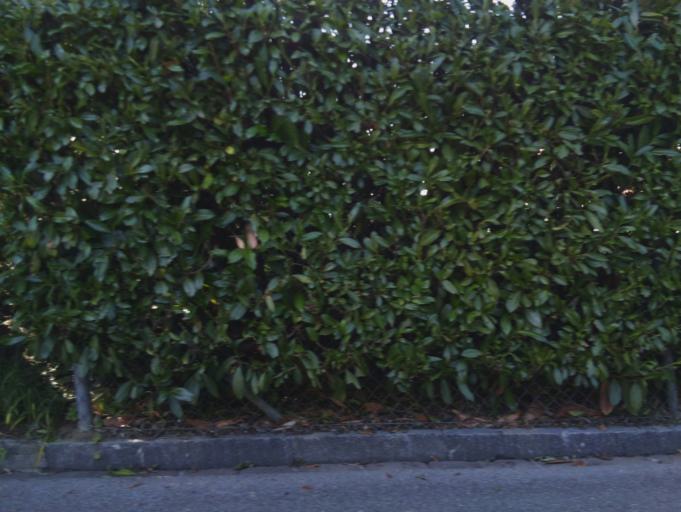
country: CH
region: Schwyz
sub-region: Bezirk March
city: Schubelbach
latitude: 47.1728
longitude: 8.9065
